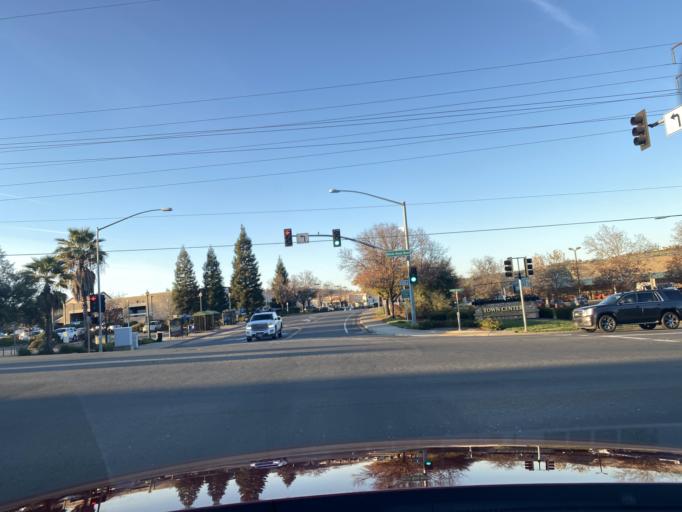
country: US
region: California
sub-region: El Dorado County
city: El Dorado Hills
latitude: 38.6473
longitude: -121.0664
